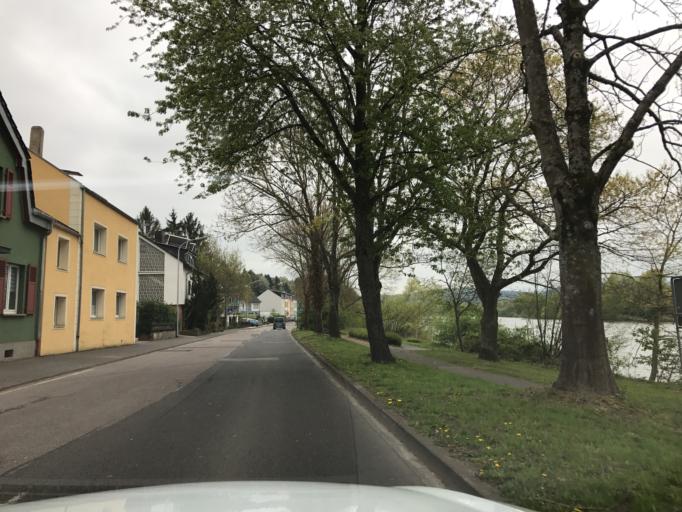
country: DE
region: Rheinland-Pfalz
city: Konz
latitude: 49.6967
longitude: 6.5705
